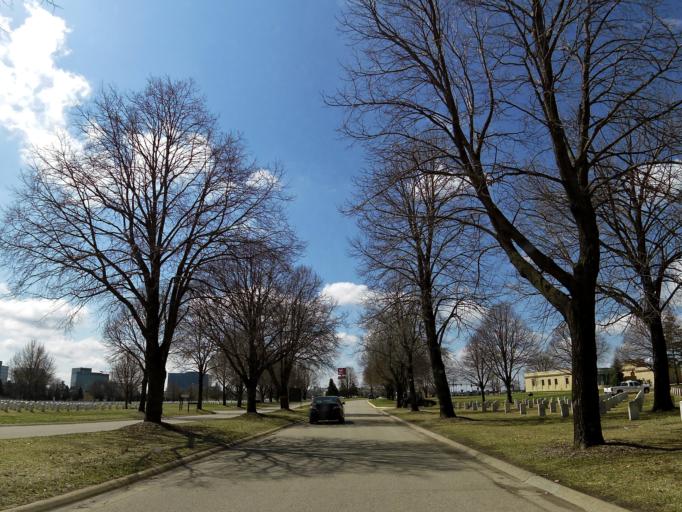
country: US
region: Minnesota
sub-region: Hennepin County
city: Richfield
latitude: 44.8656
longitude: -93.2203
